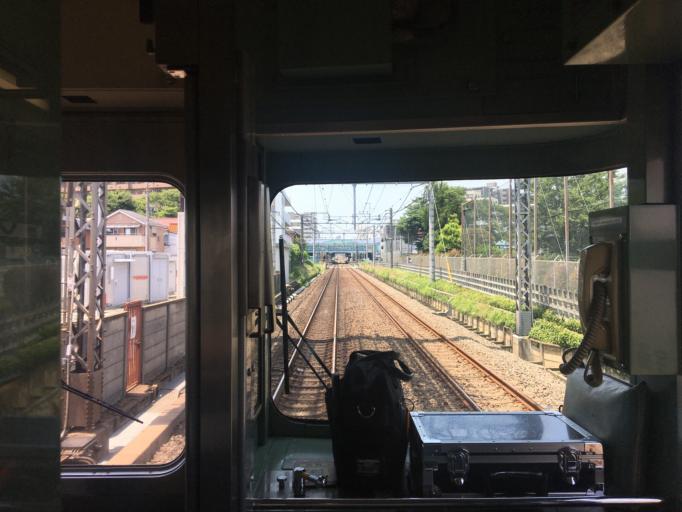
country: JP
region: Tokyo
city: Tanashicho
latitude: 35.7582
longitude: 139.5362
